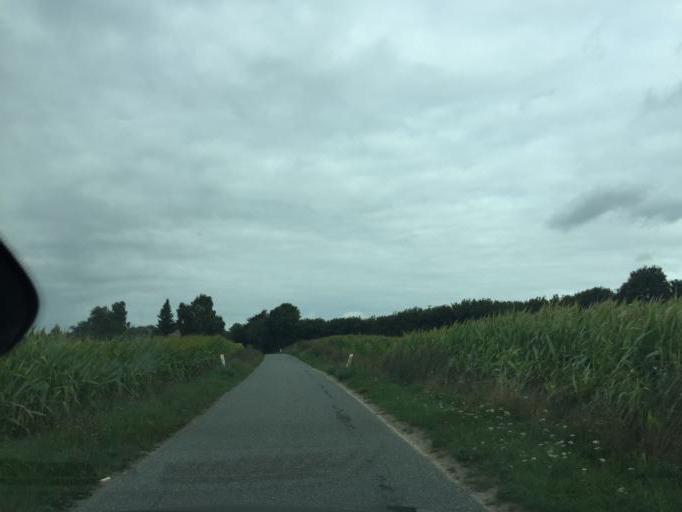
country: DK
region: South Denmark
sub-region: Assens Kommune
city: Vissenbjerg
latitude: 55.3713
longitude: 10.1215
